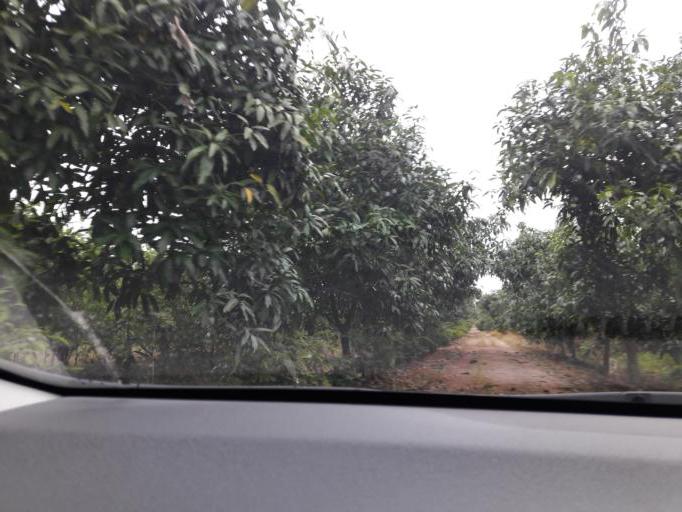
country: TH
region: Ratchaburi
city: Damnoen Saduak
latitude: 13.5774
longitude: 100.0185
